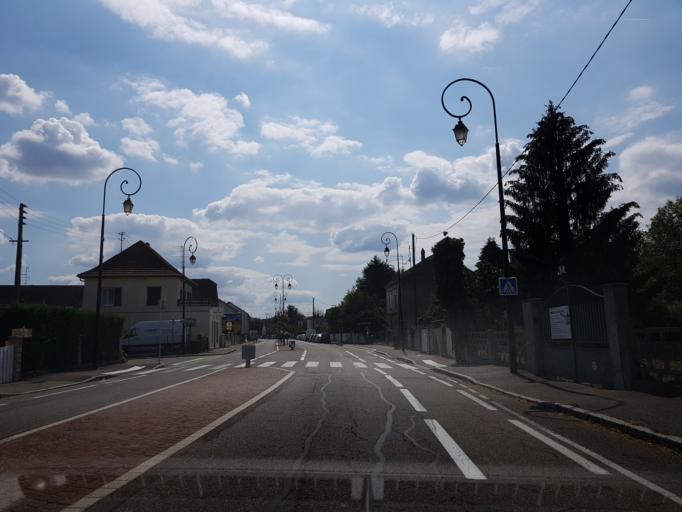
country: FR
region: Alsace
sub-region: Departement du Haut-Rhin
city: Sausheim
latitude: 47.7776
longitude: 7.3635
